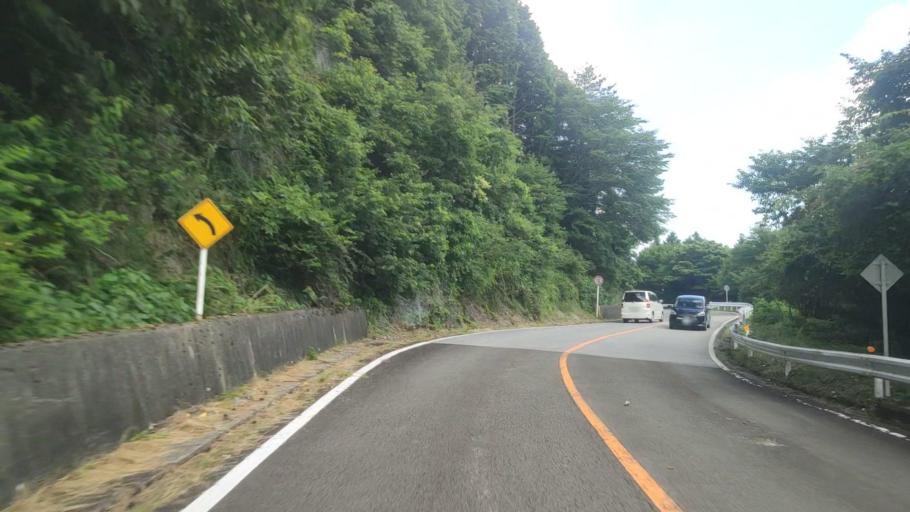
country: JP
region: Gifu
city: Tarui
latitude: 35.3987
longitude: 136.4288
